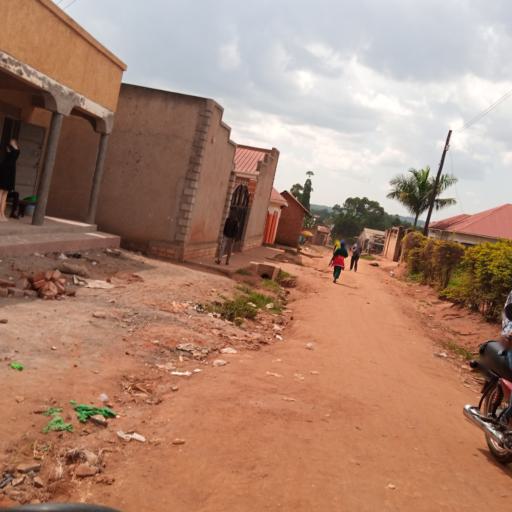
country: UG
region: Eastern Region
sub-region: Mbale District
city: Mbale
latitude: 1.0989
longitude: 34.1776
